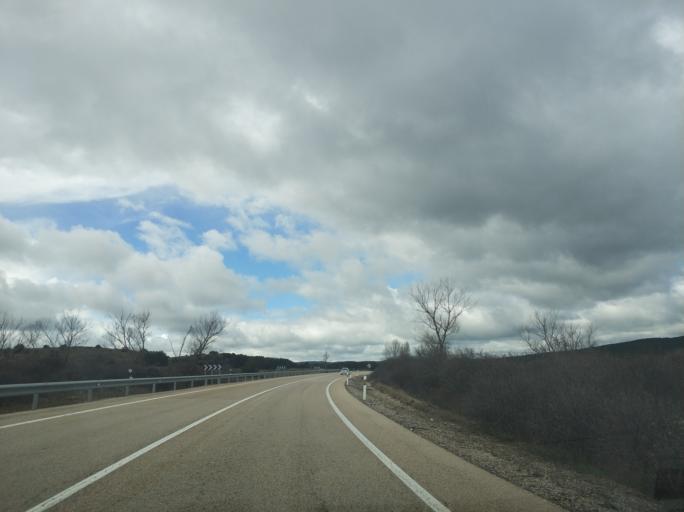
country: ES
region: Castille and Leon
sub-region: Provincia de Soria
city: Cabrejas del Pinar
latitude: 41.8040
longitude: -2.8664
